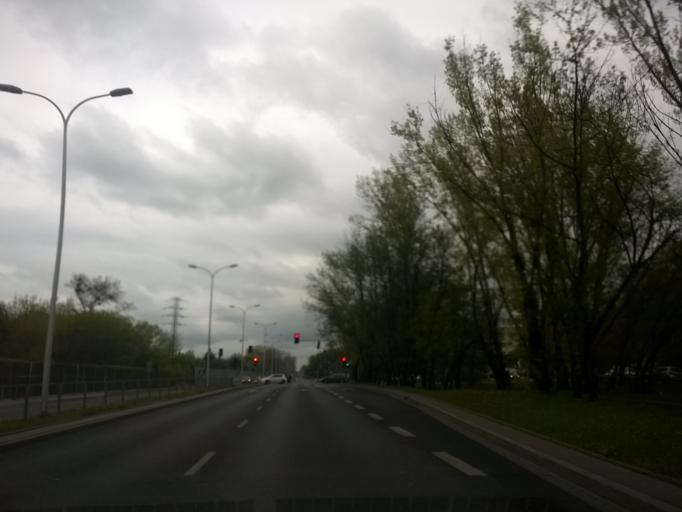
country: PL
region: Masovian Voivodeship
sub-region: Warszawa
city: Ursynow
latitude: 52.1728
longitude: 21.0543
